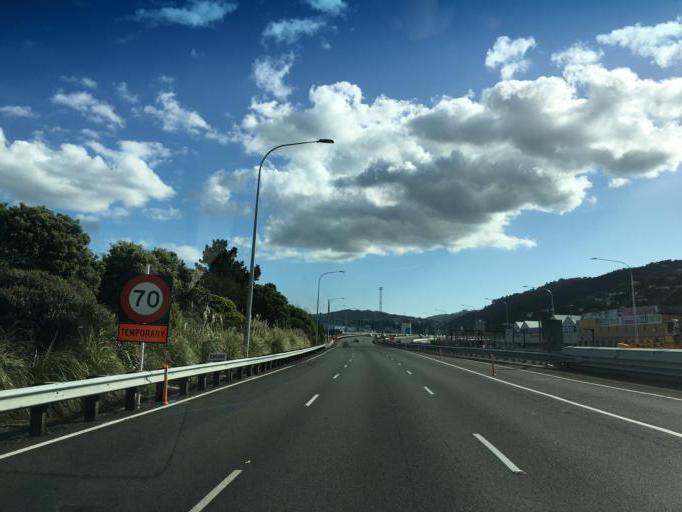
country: NZ
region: Wellington
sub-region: Wellington City
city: Wellington
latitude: -41.2593
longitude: 174.7929
